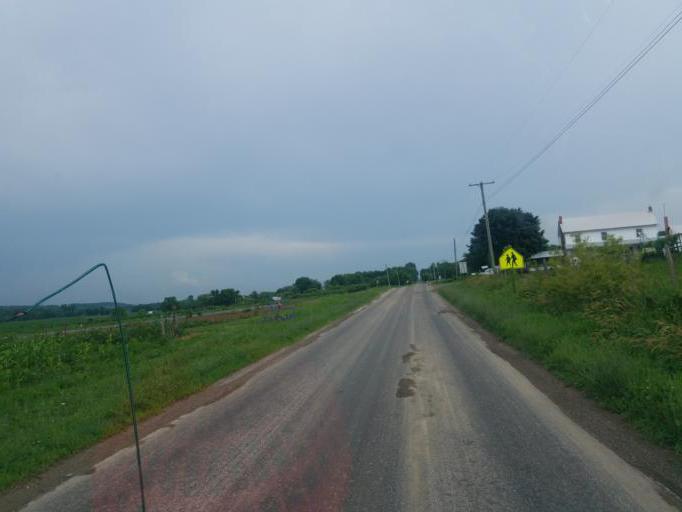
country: US
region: Ohio
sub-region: Wayne County
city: West Salem
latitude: 40.8646
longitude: -82.1533
